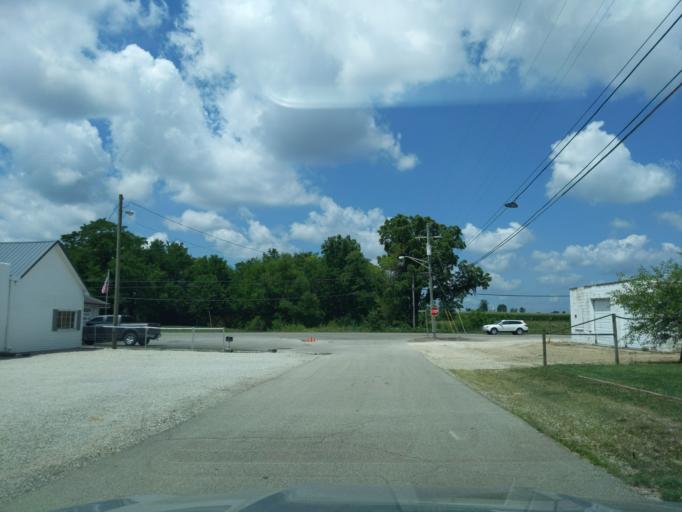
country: US
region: Indiana
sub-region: Ripley County
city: Osgood
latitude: 39.2027
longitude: -85.3299
